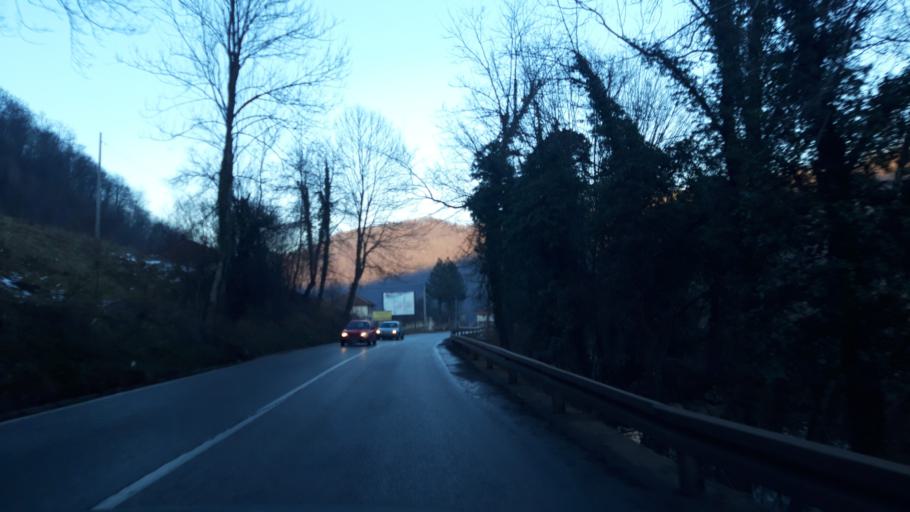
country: BA
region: Republika Srpska
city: Milici
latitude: 44.1800
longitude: 19.0741
